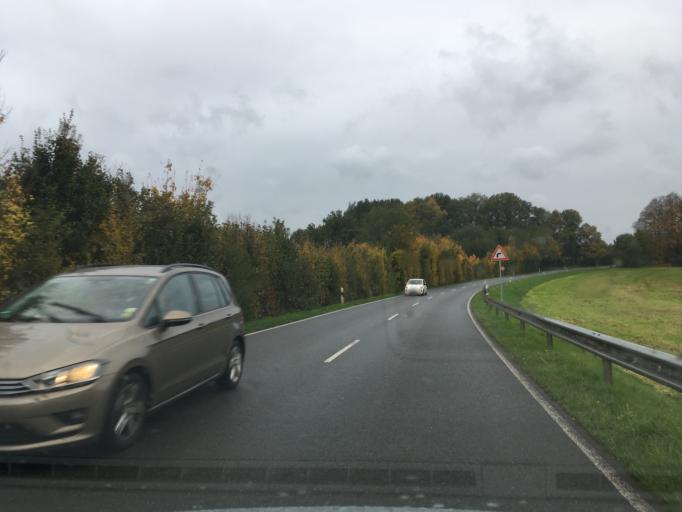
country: DE
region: North Rhine-Westphalia
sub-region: Regierungsbezirk Munster
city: Klein Reken
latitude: 51.8133
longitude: 7.1014
